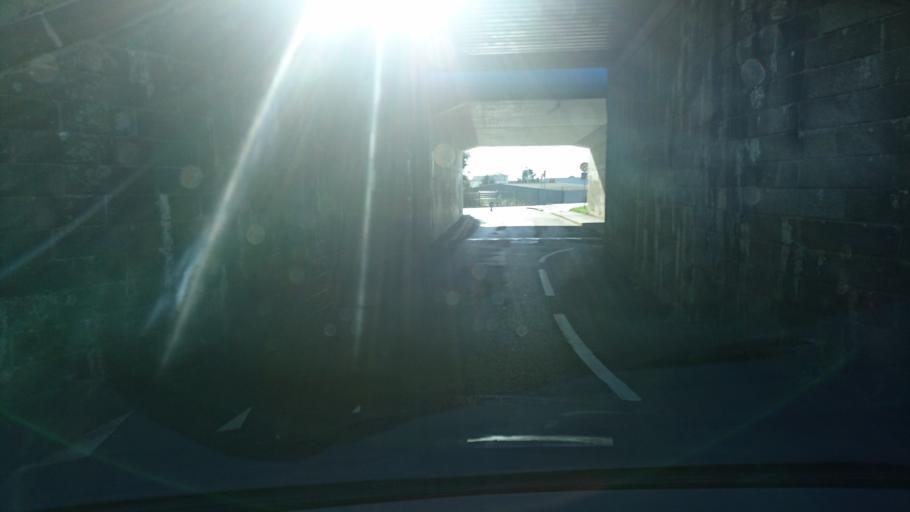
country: FR
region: Brittany
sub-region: Departement du Finistere
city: Brest
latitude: 48.3937
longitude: -4.4486
